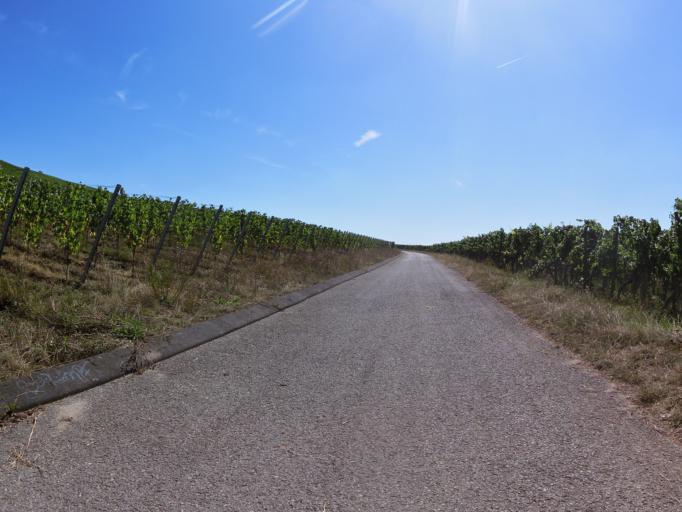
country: DE
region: Bavaria
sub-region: Regierungsbezirk Unterfranken
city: Thungersheim
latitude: 49.8732
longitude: 9.8533
